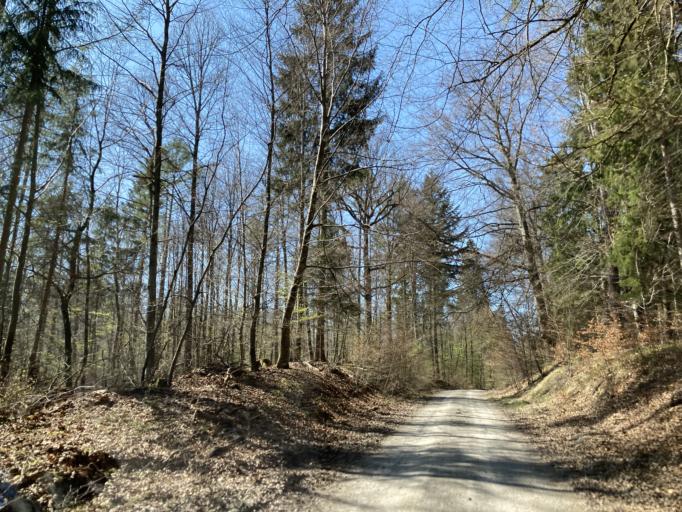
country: DE
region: Baden-Wuerttemberg
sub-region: Regierungsbezirk Stuttgart
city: Altdorf
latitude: 48.5726
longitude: 9.0052
